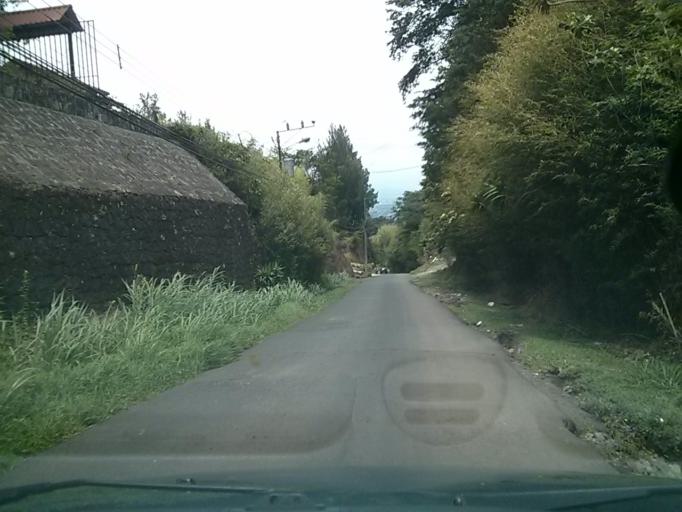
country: CR
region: Heredia
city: Santo Domingo
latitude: 10.0630
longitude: -84.1129
